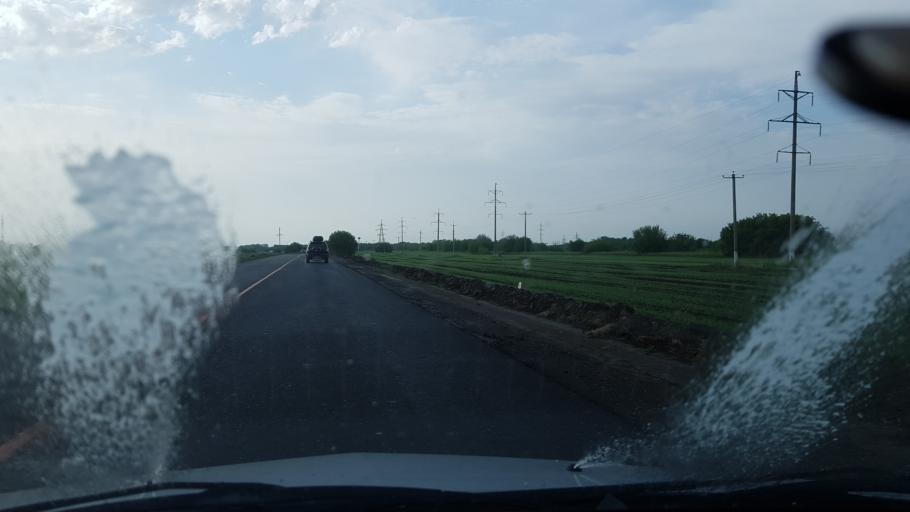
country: RU
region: Samara
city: Khryashchevka
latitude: 53.8069
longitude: 49.1147
